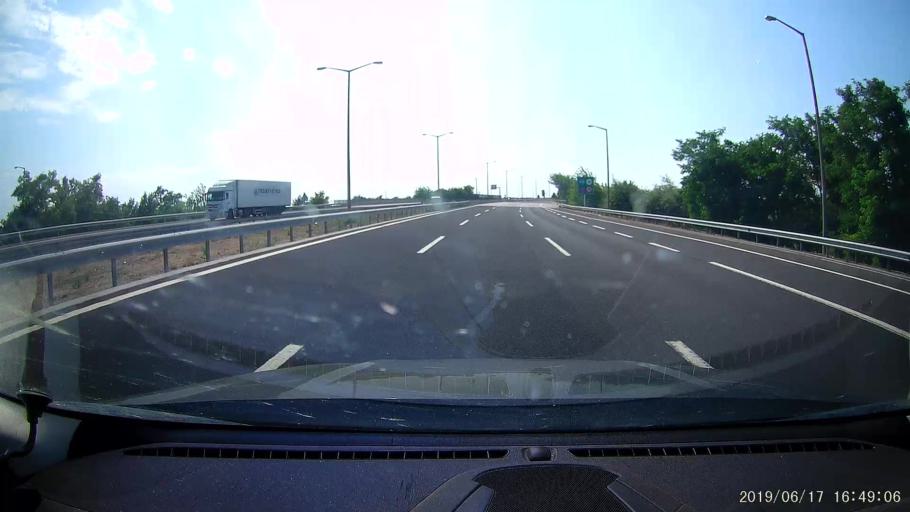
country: TR
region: Kirklareli
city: Babaeski
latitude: 41.5051
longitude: 27.1211
